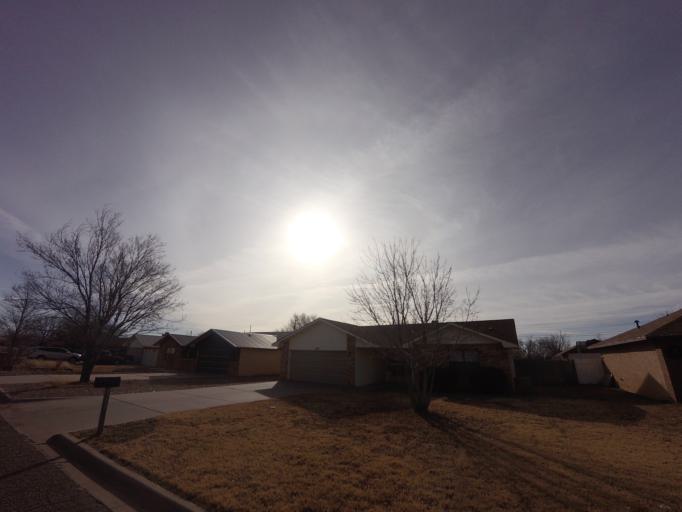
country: US
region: New Mexico
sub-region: Curry County
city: Clovis
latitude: 34.4160
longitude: -103.2299
